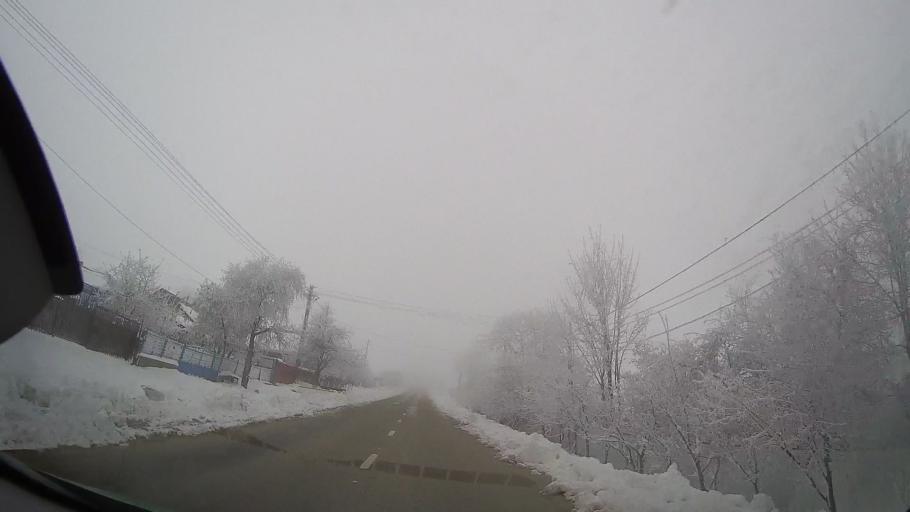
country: RO
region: Neamt
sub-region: Comuna Valea Ursului
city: Valea Ursului
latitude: 46.8001
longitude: 27.0760
